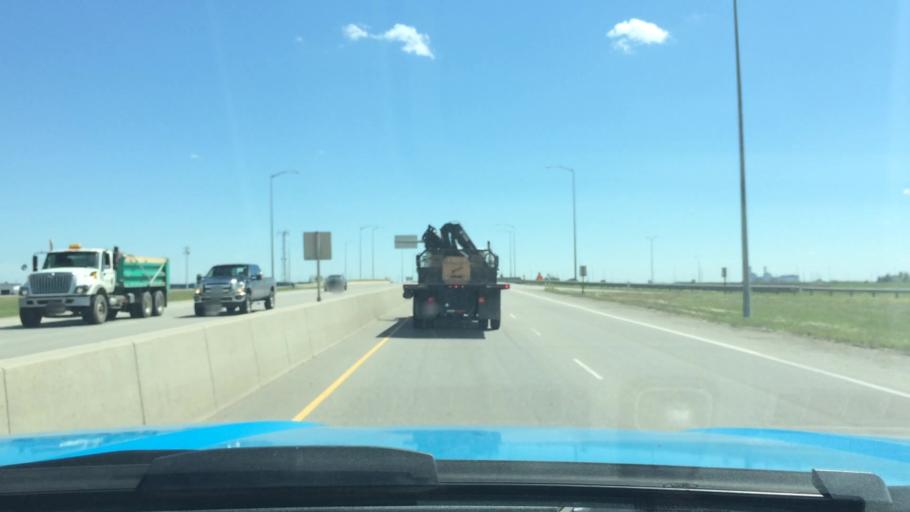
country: CA
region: Alberta
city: Chestermere
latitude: 50.9795
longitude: -113.9233
